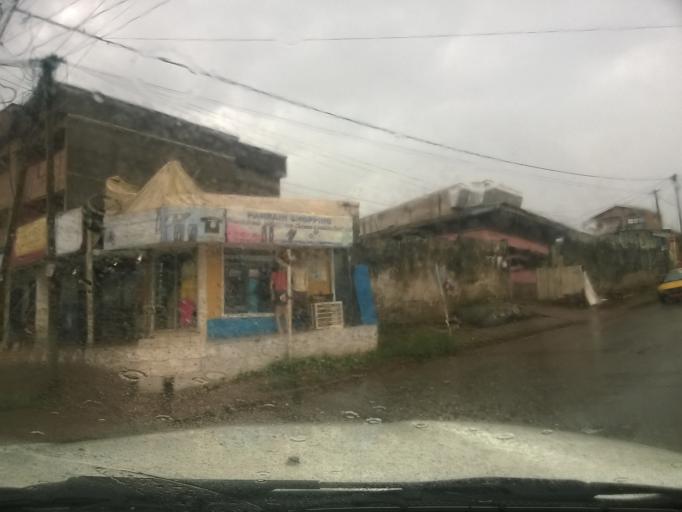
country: CM
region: Centre
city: Yaounde
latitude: 3.8749
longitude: 11.5403
